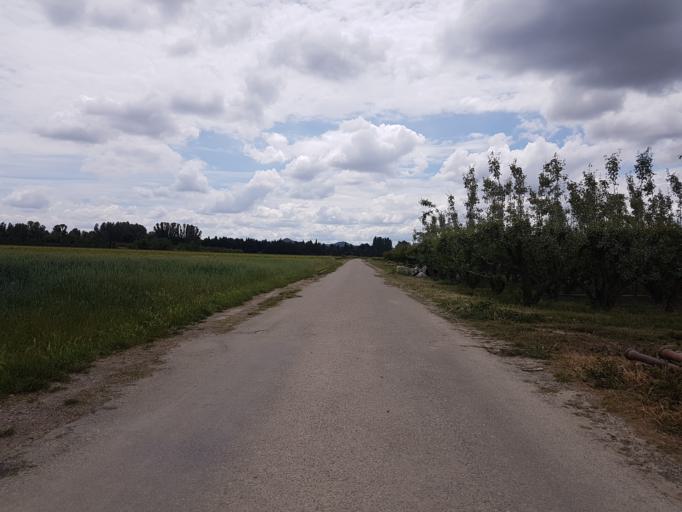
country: FR
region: Languedoc-Roussillon
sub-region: Departement du Gard
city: Vallabregues
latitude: 43.8755
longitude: 4.6259
